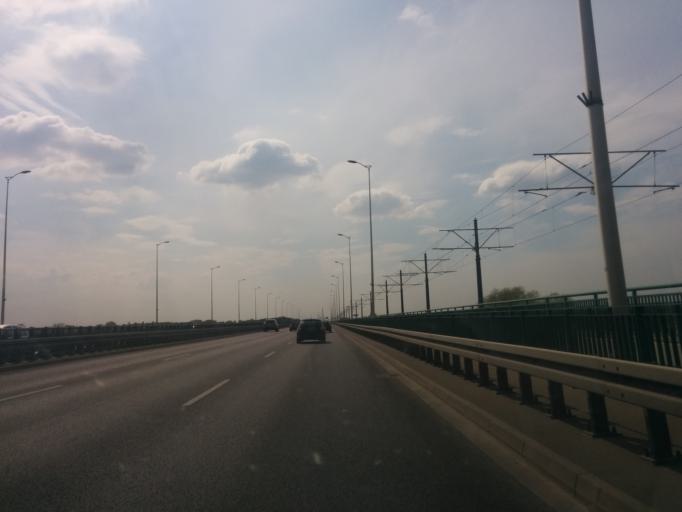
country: PL
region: Masovian Voivodeship
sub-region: Warszawa
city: Bialoleka
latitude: 52.3089
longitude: 20.9558
